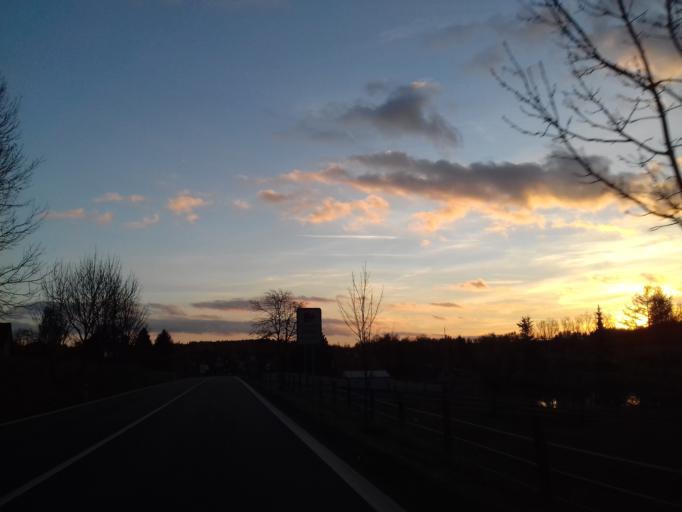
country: CZ
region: Vysocina
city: Krizova
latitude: 49.7199
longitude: 15.8625
